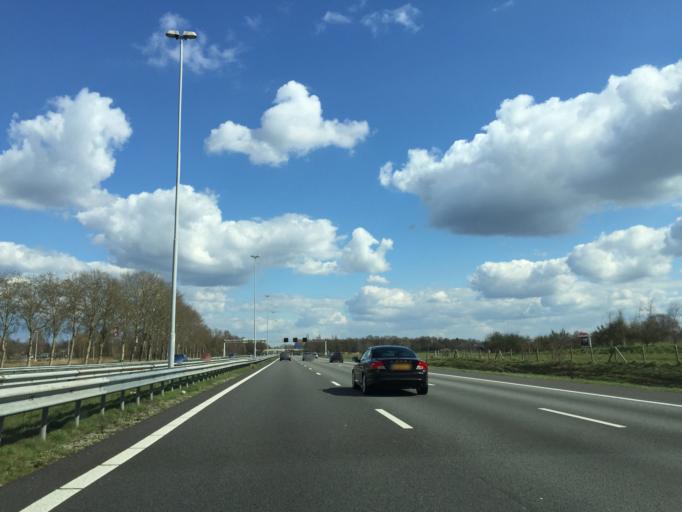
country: NL
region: North Brabant
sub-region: Gemeente Goirle
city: Goirle
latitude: 51.5371
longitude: 5.0722
